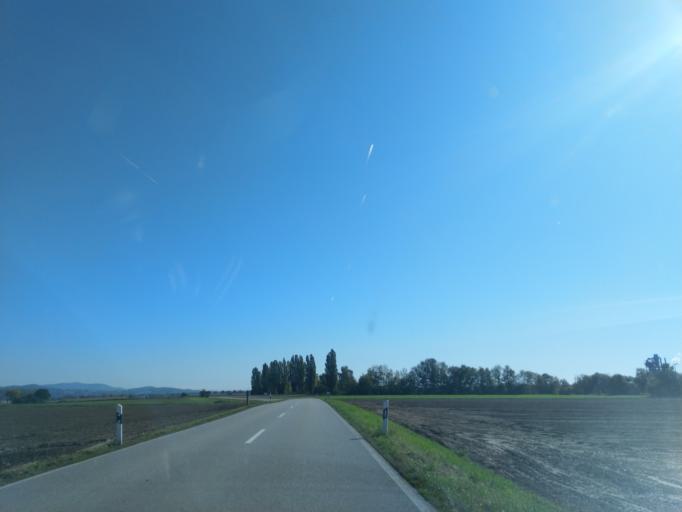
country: DE
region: Bavaria
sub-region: Lower Bavaria
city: Offenberg
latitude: 48.8227
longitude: 12.8508
